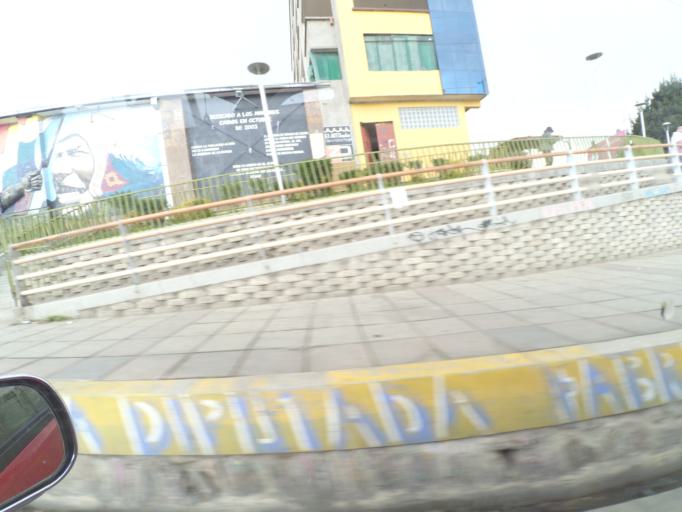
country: BO
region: La Paz
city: La Paz
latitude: -16.5020
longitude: -68.1621
